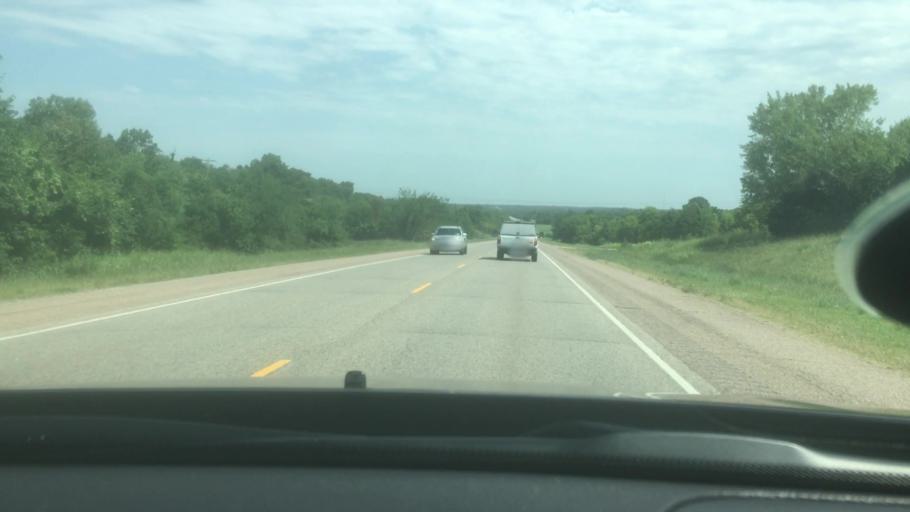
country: US
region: Oklahoma
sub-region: Seminole County
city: Maud
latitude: 35.0616
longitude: -96.9314
